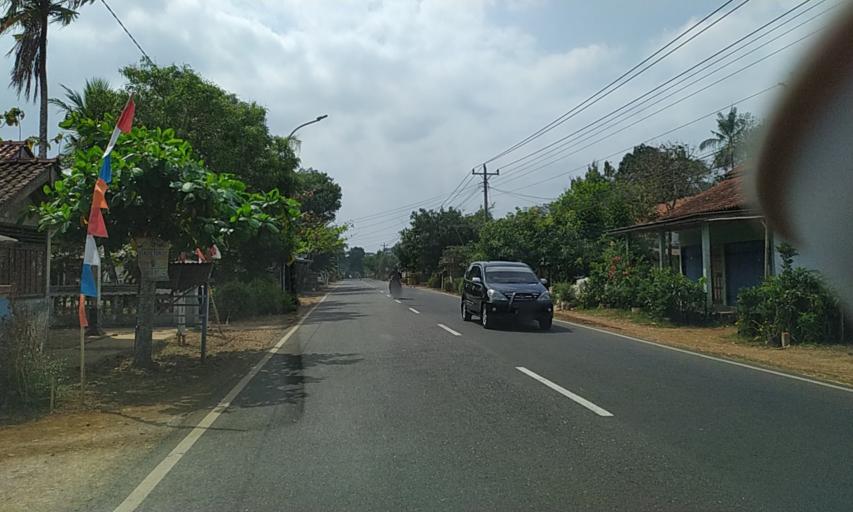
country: ID
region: Central Java
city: Kroya
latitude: -7.6430
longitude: 109.3192
